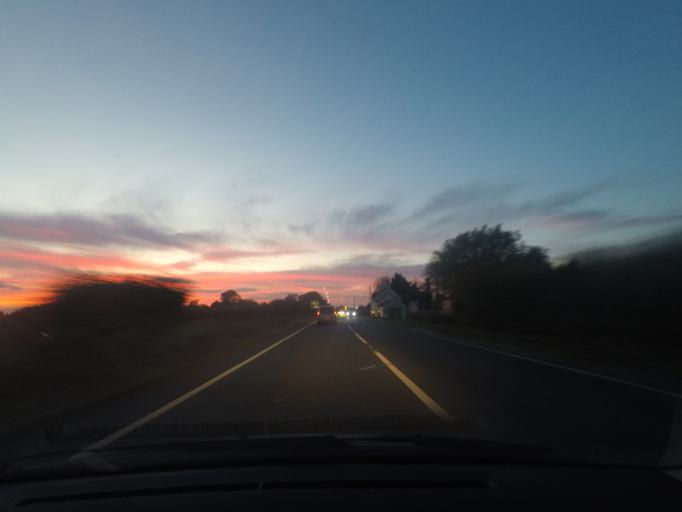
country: GB
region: England
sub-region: East Riding of Yorkshire
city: Thornton
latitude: 53.9322
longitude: -0.8339
